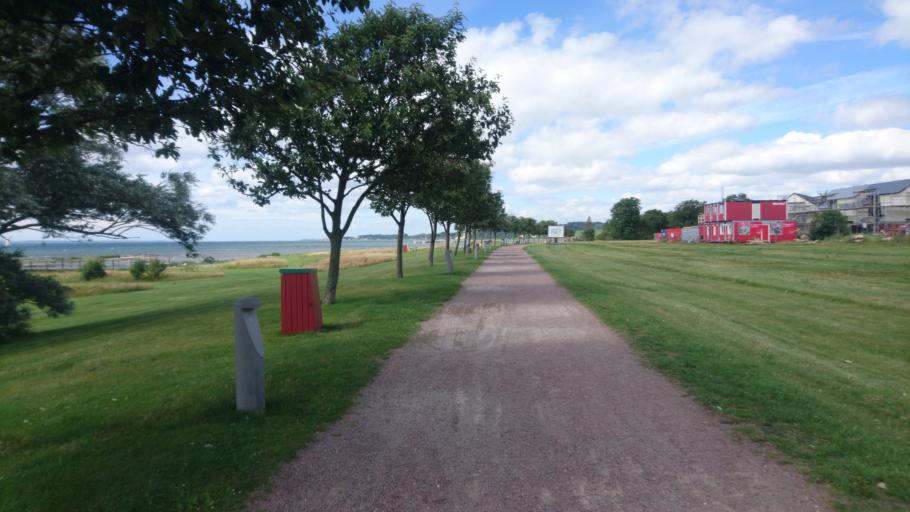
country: SE
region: Skane
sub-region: Landskrona
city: Landskrona
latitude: 55.9001
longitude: 12.8042
